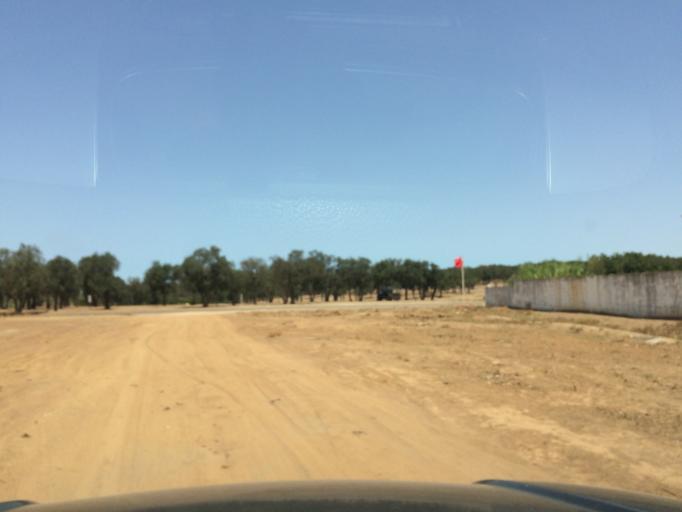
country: MA
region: Chaouia-Ouardigha
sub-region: Benslimane
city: Mellila
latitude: 33.5652
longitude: -6.9003
